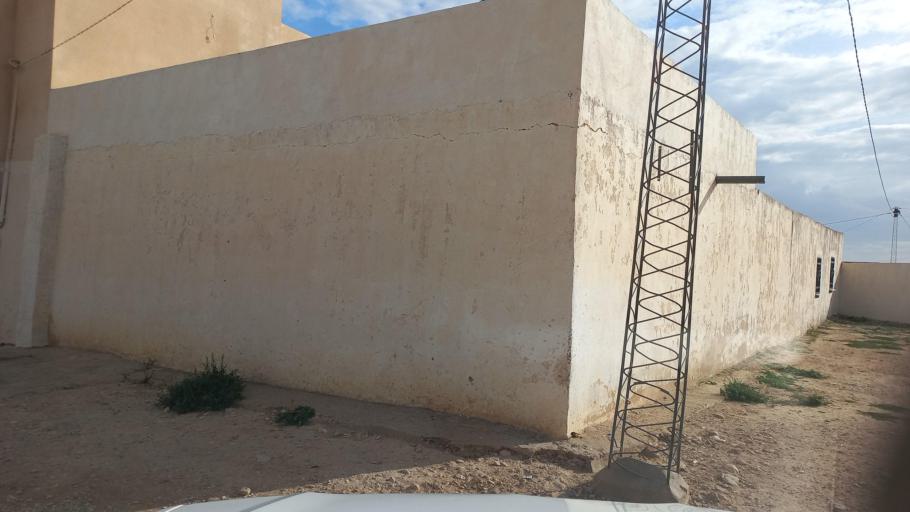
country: TN
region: Al Qasrayn
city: Sbiba
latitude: 35.4460
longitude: 9.0758
